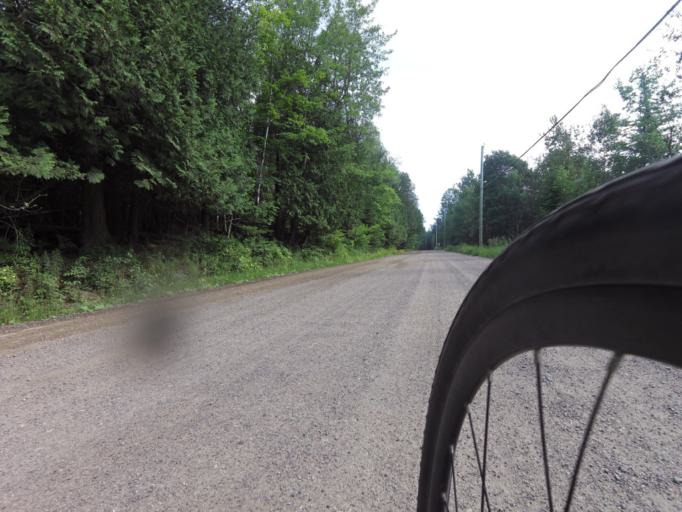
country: CA
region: Quebec
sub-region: Laurentides
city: Mont-Tremblant
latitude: 45.9237
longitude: -74.6023
